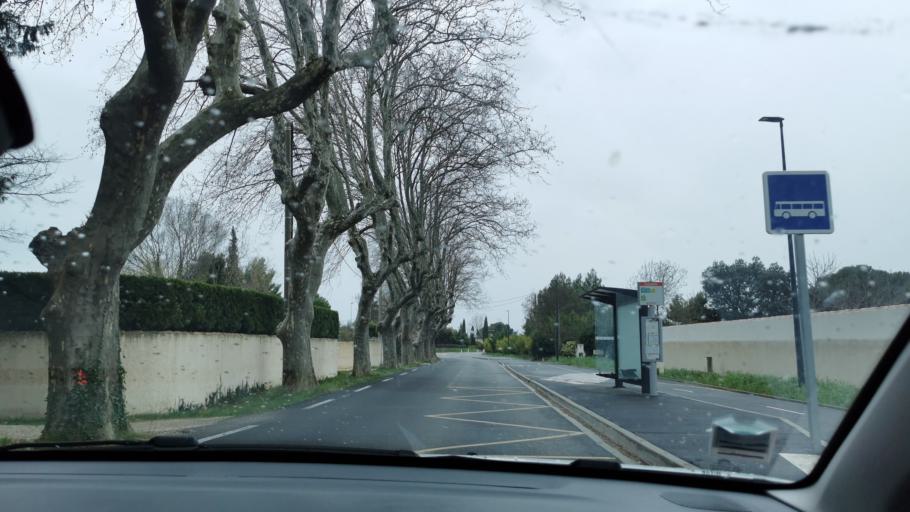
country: FR
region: Provence-Alpes-Cote d'Azur
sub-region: Departement des Bouches-du-Rhone
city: Pelissanne
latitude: 43.6298
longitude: 5.1682
